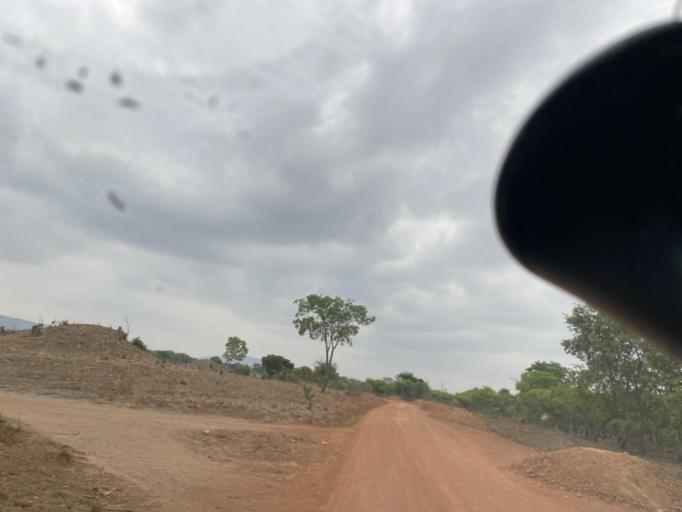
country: ZM
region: Lusaka
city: Chongwe
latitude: -15.2346
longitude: 28.7204
